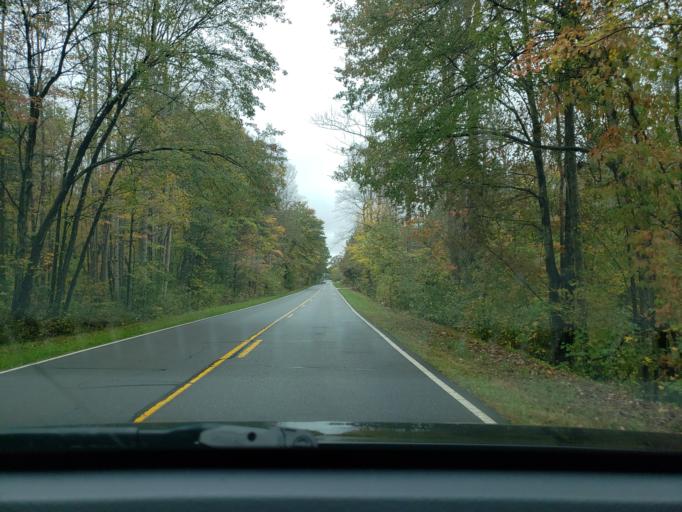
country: US
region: North Carolina
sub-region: Stokes County
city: Walnut Cove
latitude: 36.2731
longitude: -80.1445
